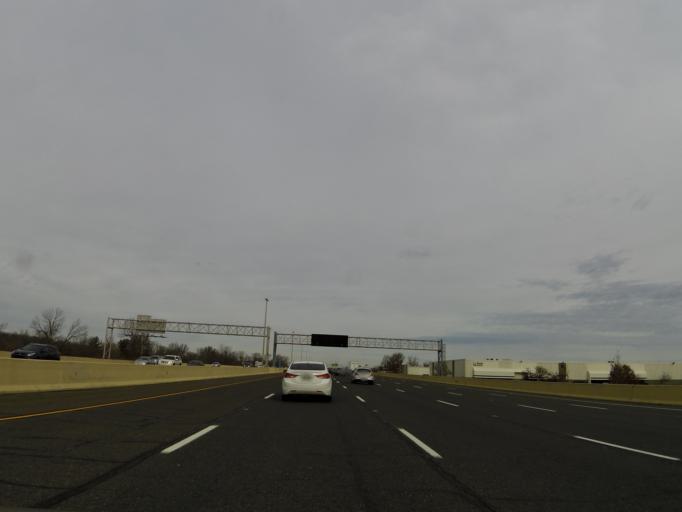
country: US
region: Indiana
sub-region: Boone County
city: Zionsville
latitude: 39.8970
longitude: -86.2696
